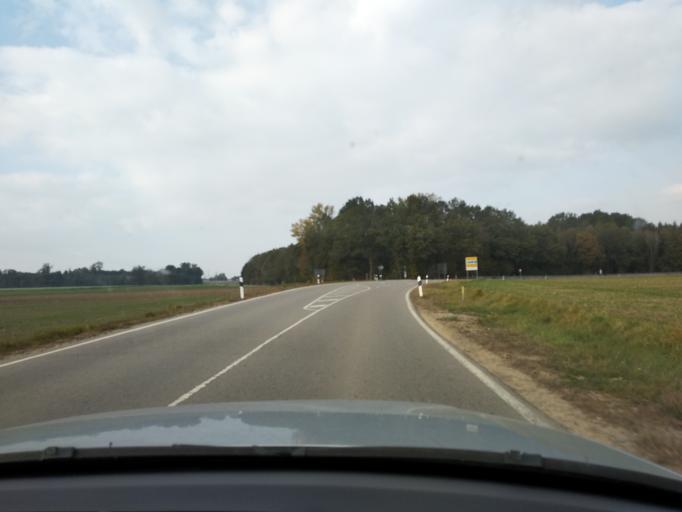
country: DE
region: Bavaria
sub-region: Upper Bavaria
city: Ottenhofen
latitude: 48.2213
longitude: 11.8783
